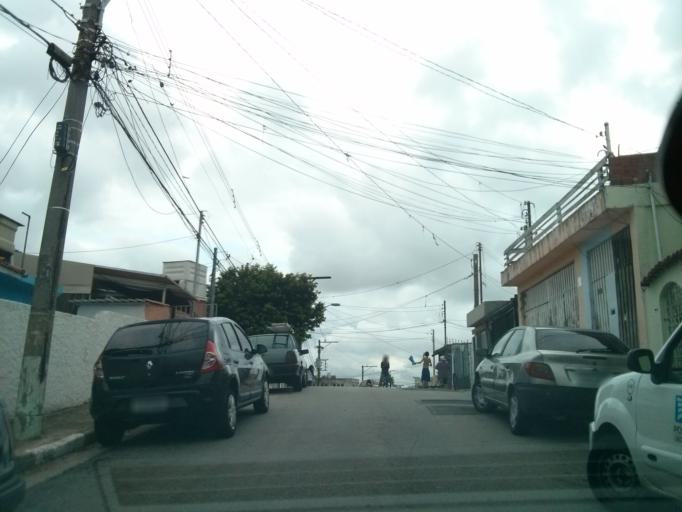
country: BR
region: Sao Paulo
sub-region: Sao Caetano Do Sul
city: Sao Caetano do Sul
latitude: -23.6091
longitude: -46.6146
